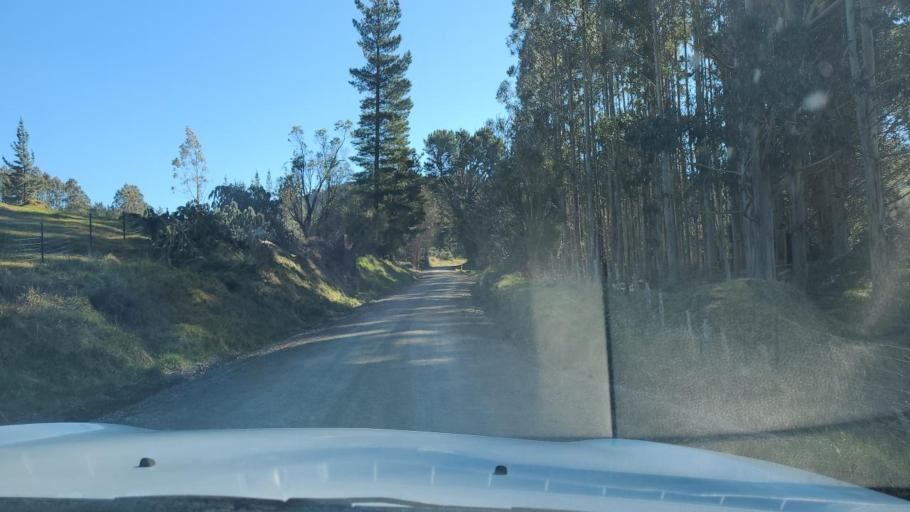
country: NZ
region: Hawke's Bay
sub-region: Napier City
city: Taradale
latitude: -39.2577
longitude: 176.5384
